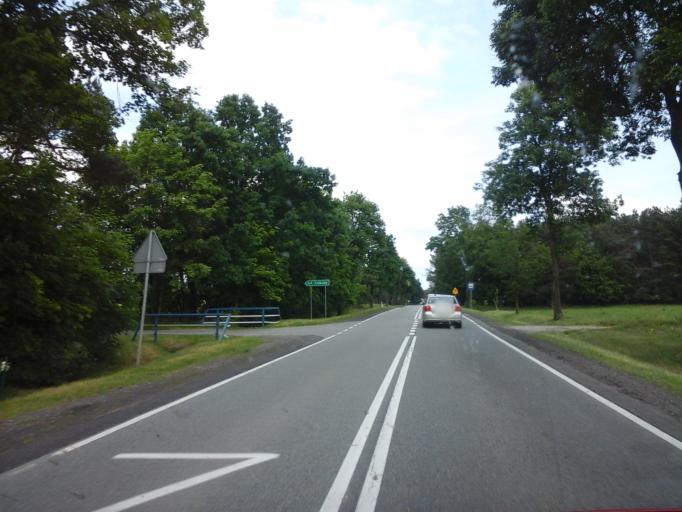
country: PL
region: Lodz Voivodeship
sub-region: Powiat opoczynski
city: Paradyz
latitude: 51.3121
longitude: 20.0826
